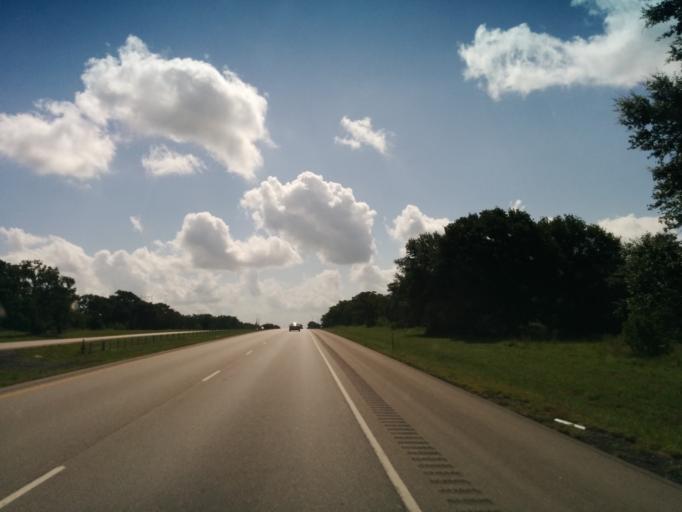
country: US
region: Texas
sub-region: Colorado County
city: Columbus
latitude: 29.6932
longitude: -96.6184
